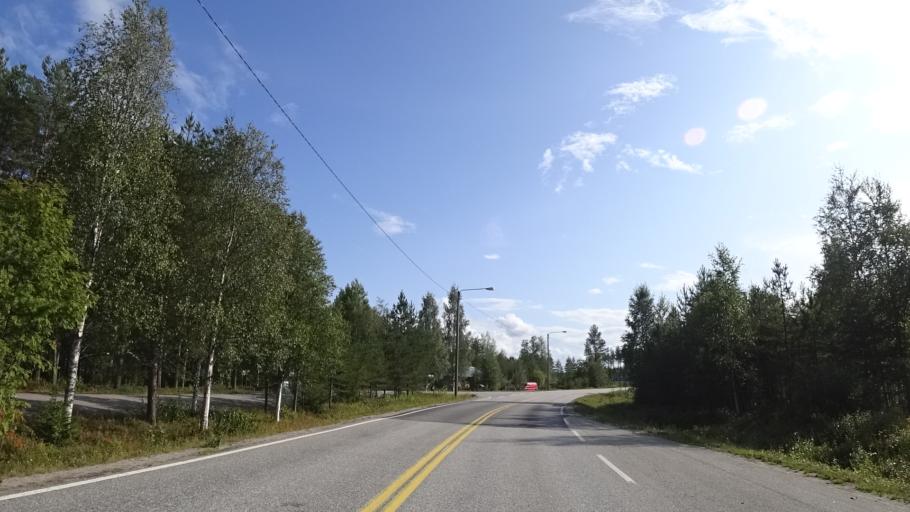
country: FI
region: North Karelia
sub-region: Pielisen Karjala
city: Lieksa
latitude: 63.4200
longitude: 30.1049
